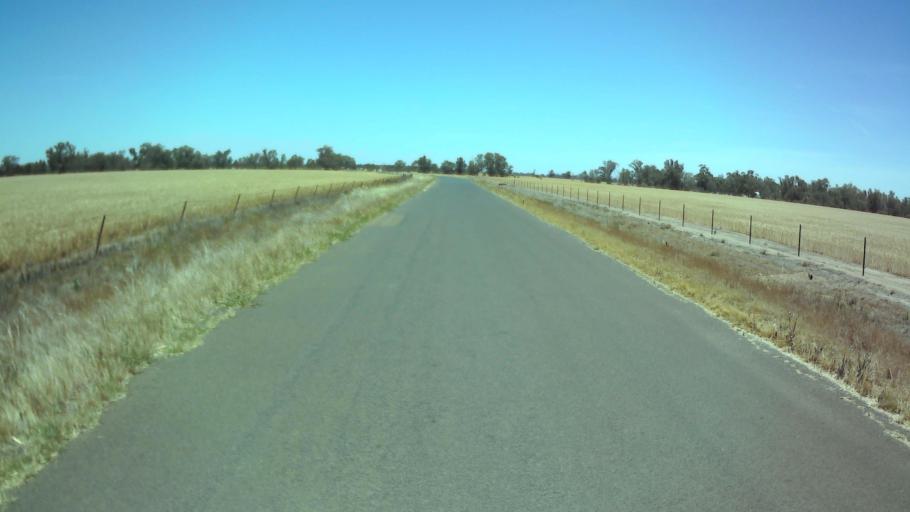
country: AU
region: New South Wales
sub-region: Weddin
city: Grenfell
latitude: -34.0336
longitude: 147.7901
